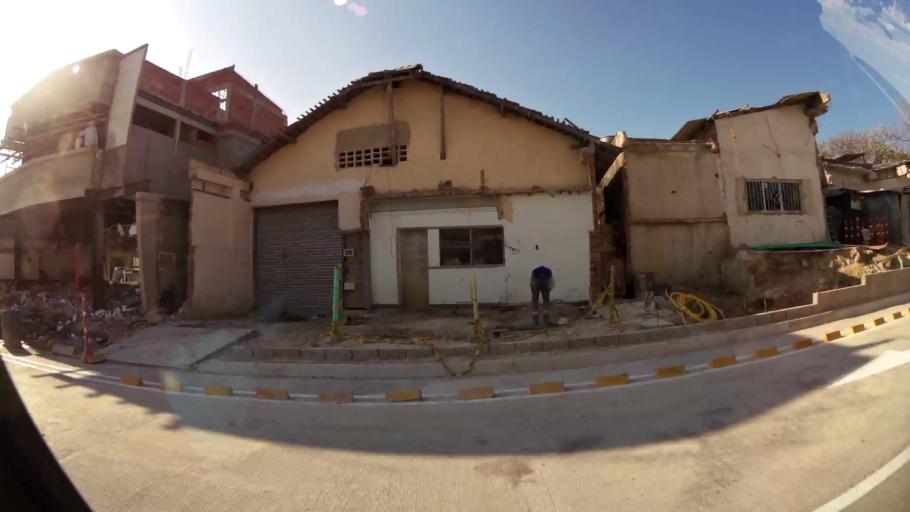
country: CO
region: Atlantico
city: Barranquilla
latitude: 10.9907
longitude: -74.7910
